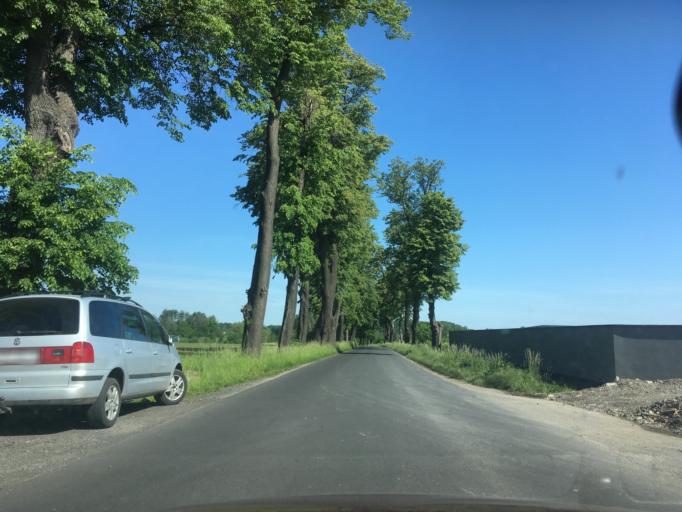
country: PL
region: Lower Silesian Voivodeship
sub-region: Powiat zgorzelecki
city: Sulikow
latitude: 51.1052
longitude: 15.0364
